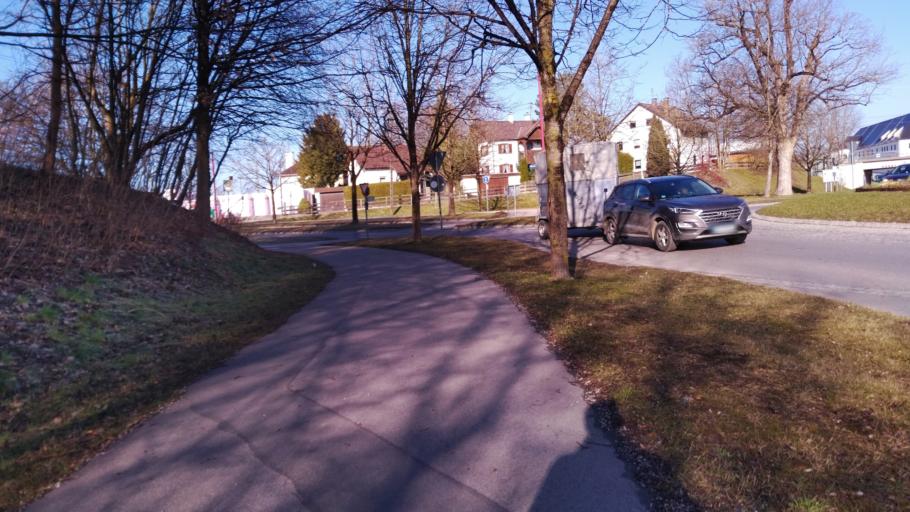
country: DE
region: Bavaria
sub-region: Upper Bavaria
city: Weilheim
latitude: 47.8484
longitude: 11.1479
